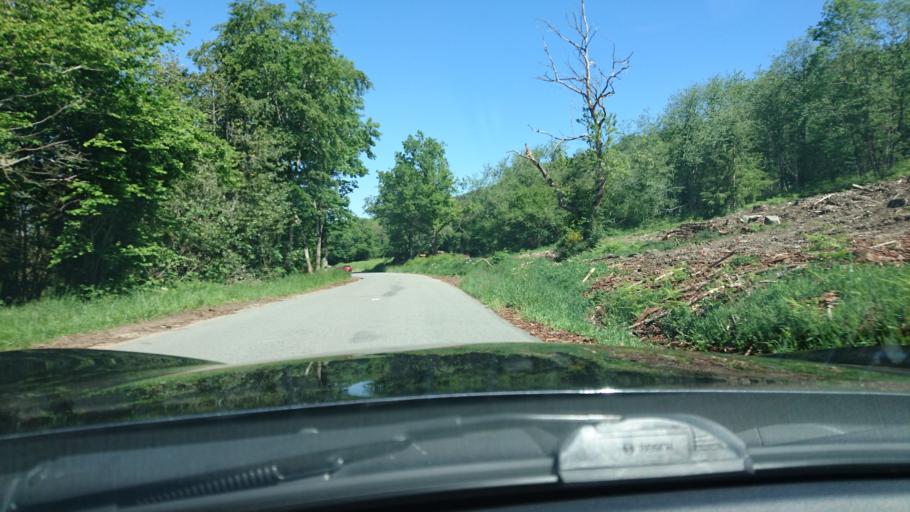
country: FR
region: Rhone-Alpes
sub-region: Departement de la Loire
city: Violay
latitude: 45.8963
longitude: 4.3170
